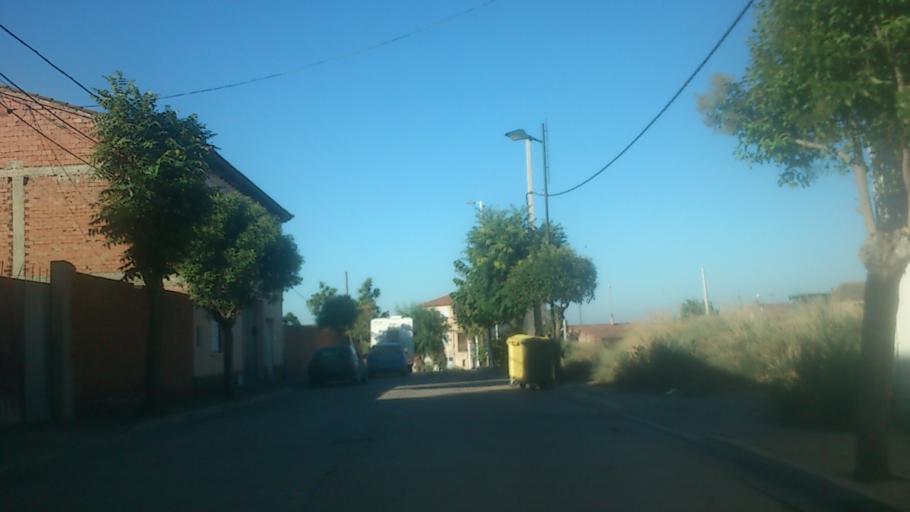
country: ES
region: Aragon
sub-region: Provincia de Zaragoza
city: San Mateo de Gallego
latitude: 41.8281
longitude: -0.7665
